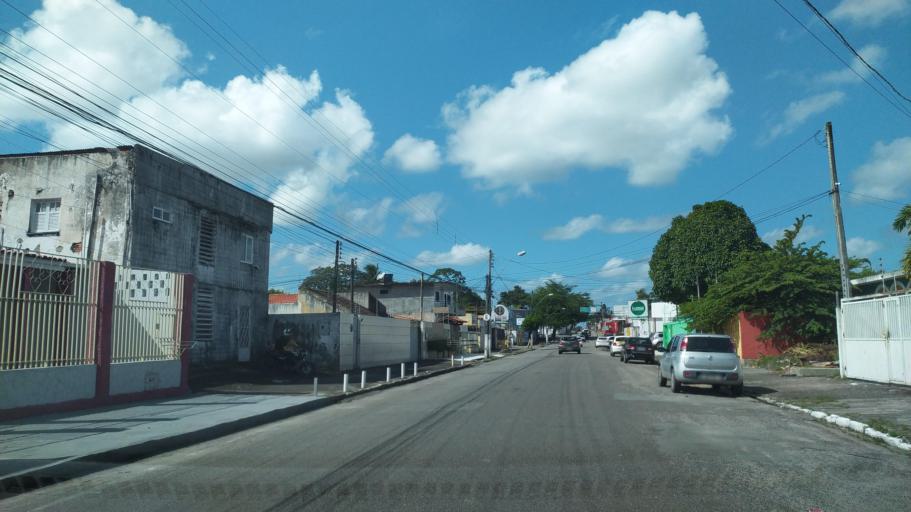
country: BR
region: Alagoas
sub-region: Maceio
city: Maceio
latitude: -9.6371
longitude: -35.7377
